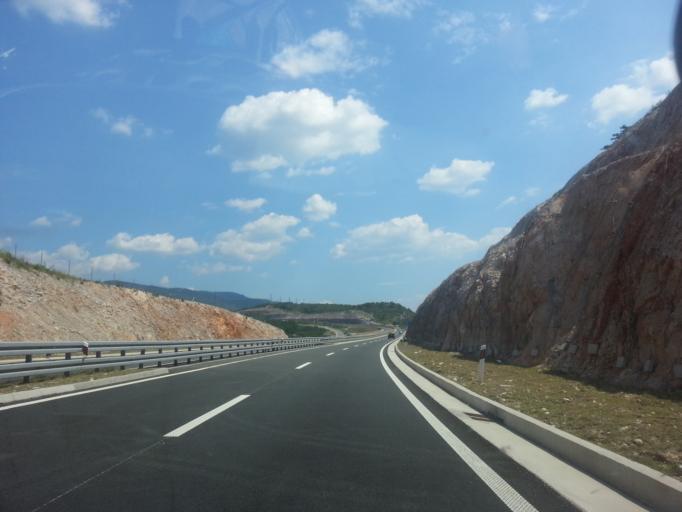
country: HR
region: Primorsko-Goranska
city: Krasica
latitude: 45.2967
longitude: 14.5699
